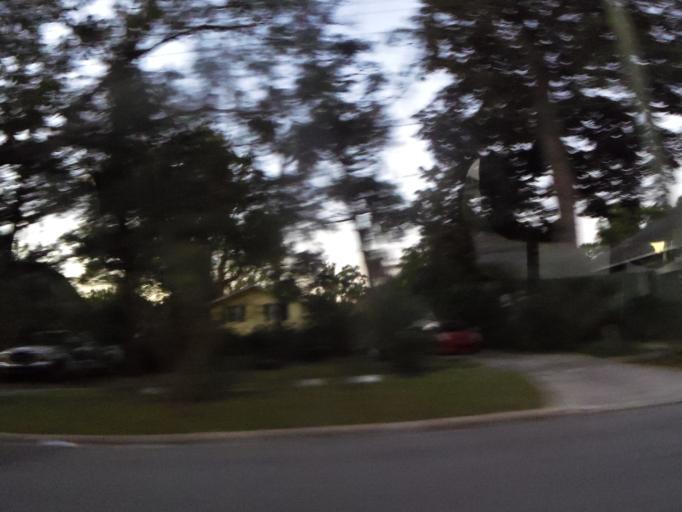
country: US
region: Florida
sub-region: Duval County
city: Jacksonville
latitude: 30.2884
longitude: -81.7166
